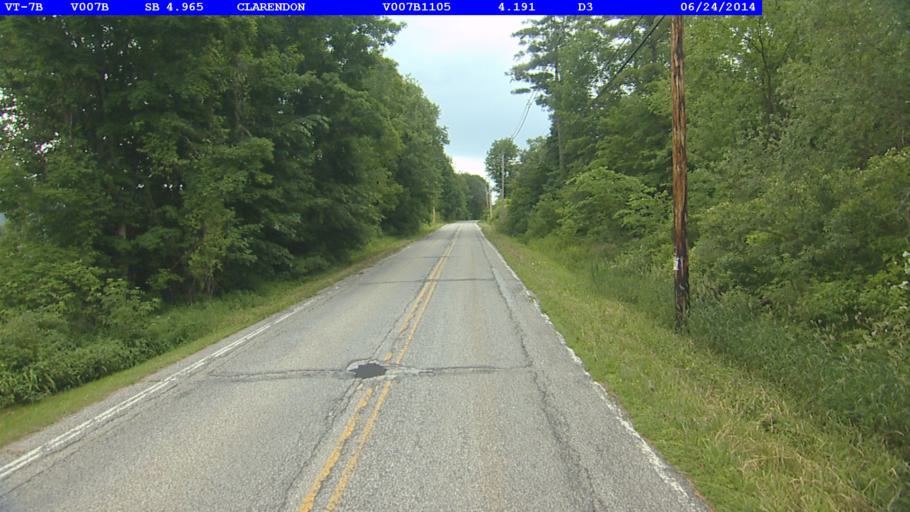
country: US
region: Vermont
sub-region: Rutland County
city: Rutland
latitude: 43.5580
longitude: -72.9621
